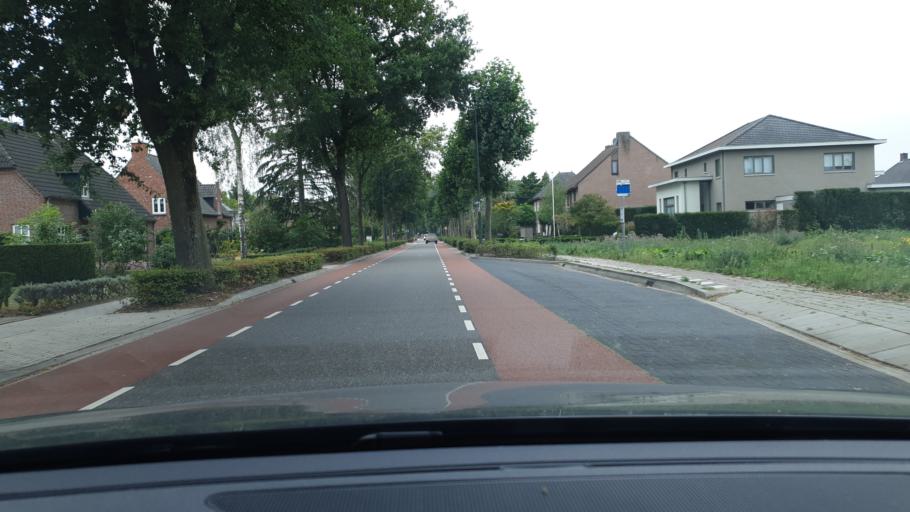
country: NL
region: North Brabant
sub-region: Gemeente Bladel en Netersel
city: Bladel
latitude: 51.3699
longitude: 5.2658
